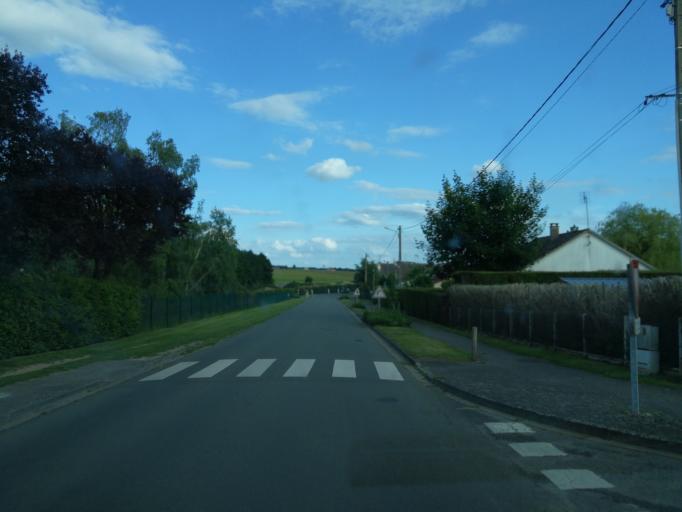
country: FR
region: Haute-Normandie
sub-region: Departement de l'Eure
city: Damville
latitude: 48.8650
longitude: 1.0717
